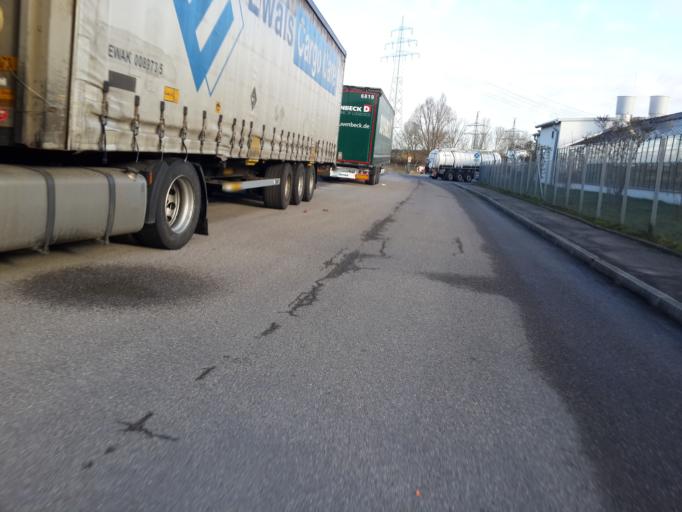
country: DE
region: Baden-Wuerttemberg
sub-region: Regierungsbezirk Stuttgart
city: Untereisesheim
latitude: 49.2058
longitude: 9.2178
